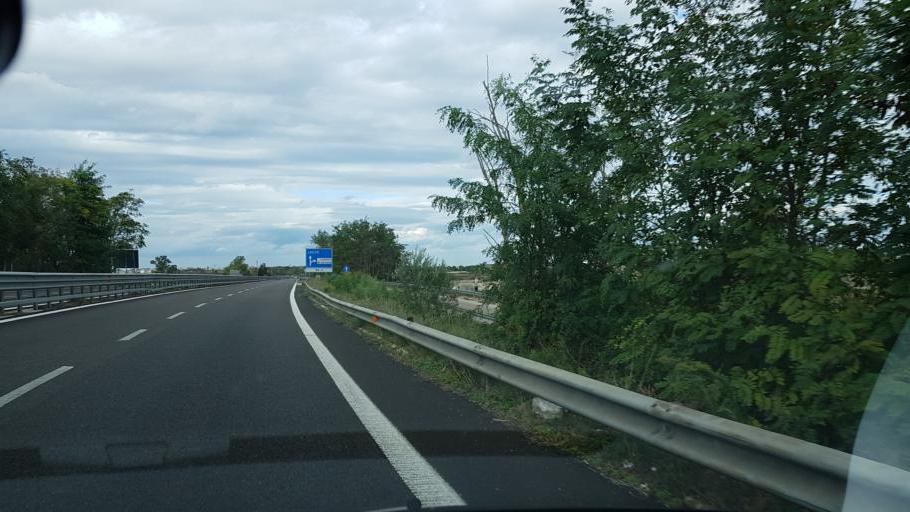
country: IT
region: Apulia
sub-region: Provincia di Lecce
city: Castromediano
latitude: 40.3278
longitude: 18.1858
